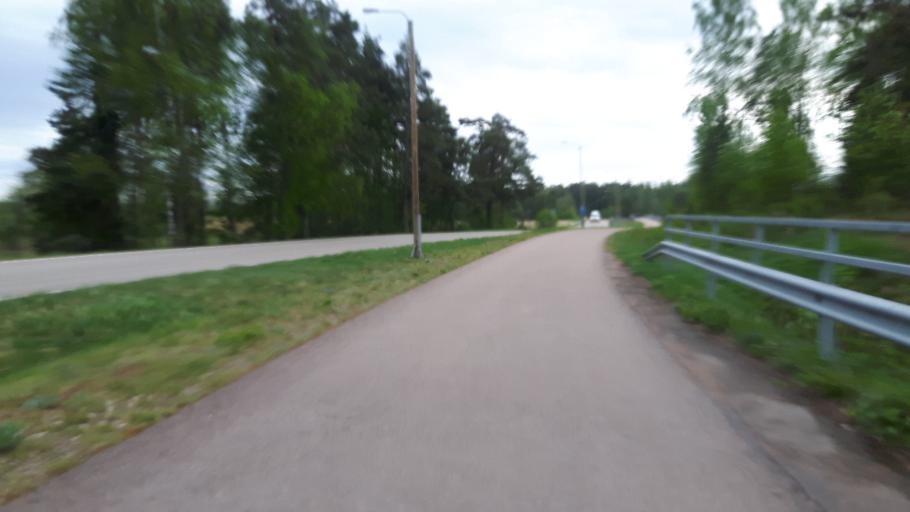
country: FI
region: Kymenlaakso
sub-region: Kotka-Hamina
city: Hamina
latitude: 60.5519
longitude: 27.2295
